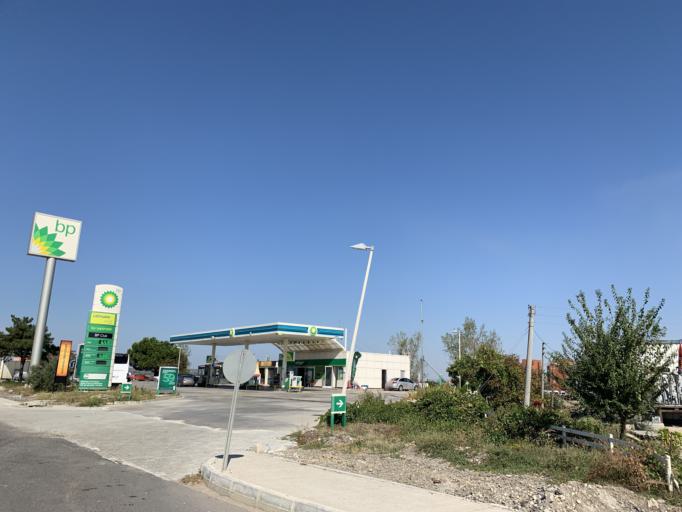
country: TR
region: Edirne
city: Ipsala
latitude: 40.9079
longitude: 26.3723
